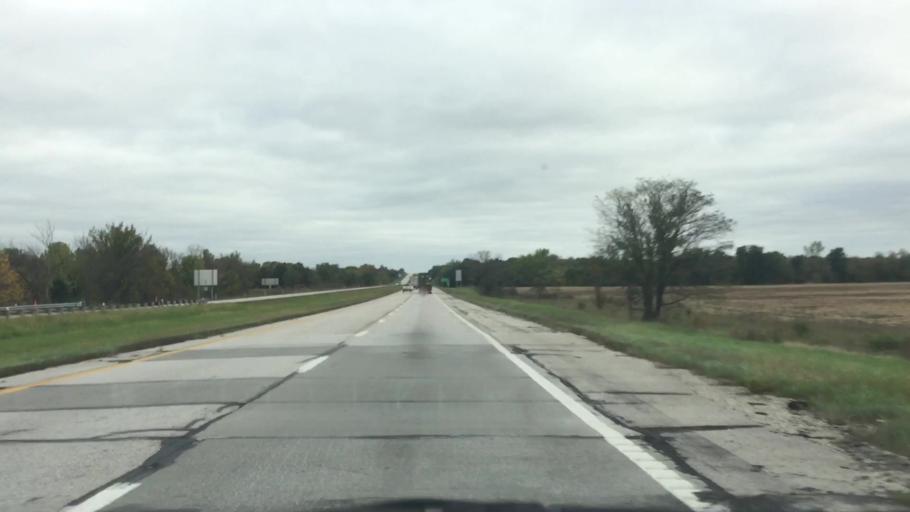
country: US
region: Missouri
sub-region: Clinton County
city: Cameron
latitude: 39.6738
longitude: -94.2341
